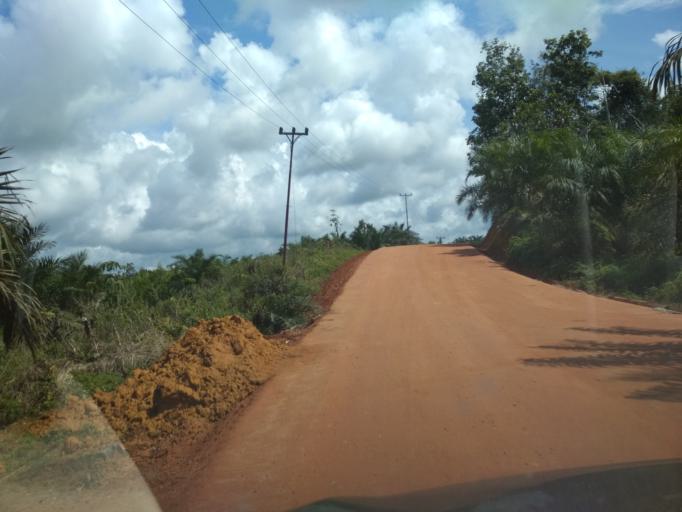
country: ID
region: West Kalimantan
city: Tayan
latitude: 0.5445
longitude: 110.0903
